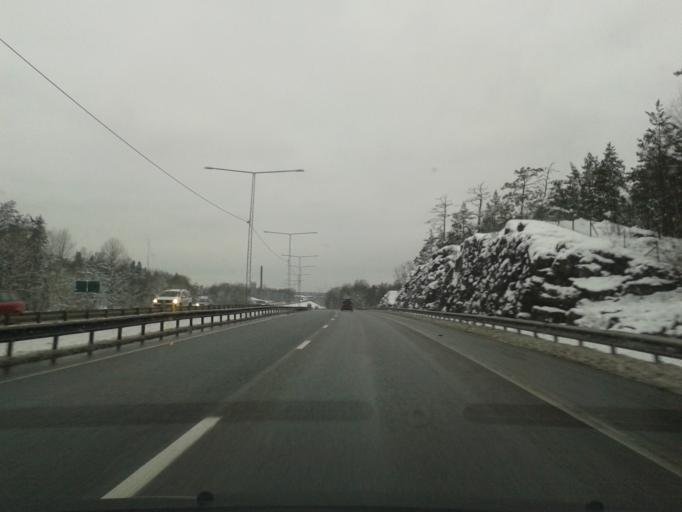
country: SE
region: Stockholm
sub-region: Nacka Kommun
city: Alta
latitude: 59.2597
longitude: 18.1629
